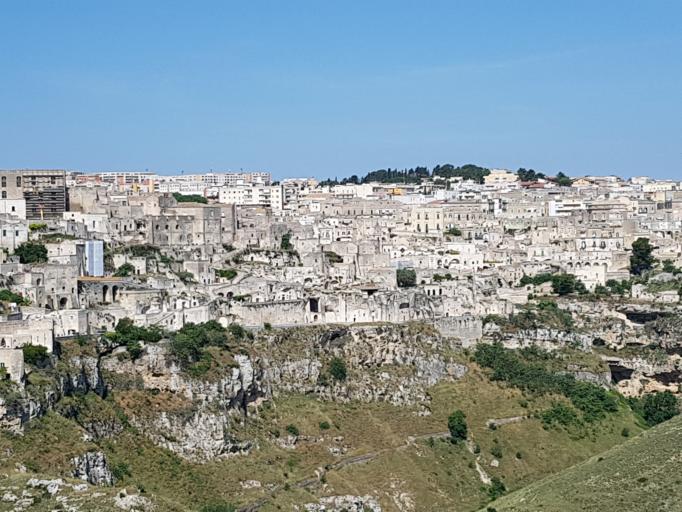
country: IT
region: Basilicate
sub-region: Provincia di Matera
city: Matera
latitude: 40.6672
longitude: 16.6183
